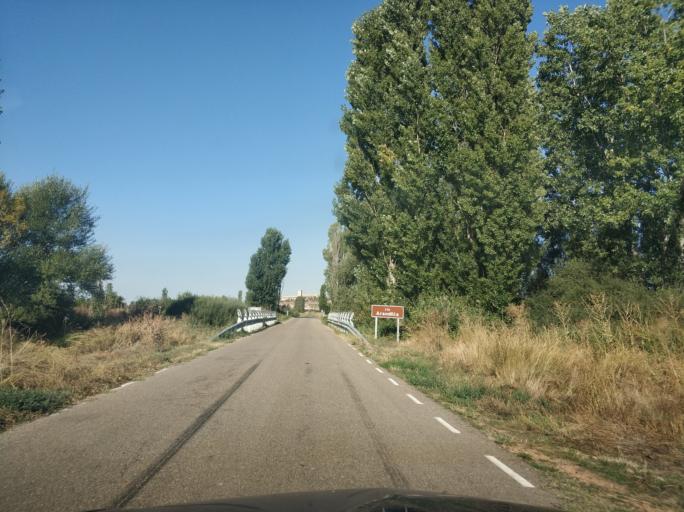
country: ES
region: Castille and Leon
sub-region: Provincia de Burgos
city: Penaranda de Duero
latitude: 41.6880
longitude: -3.4618
